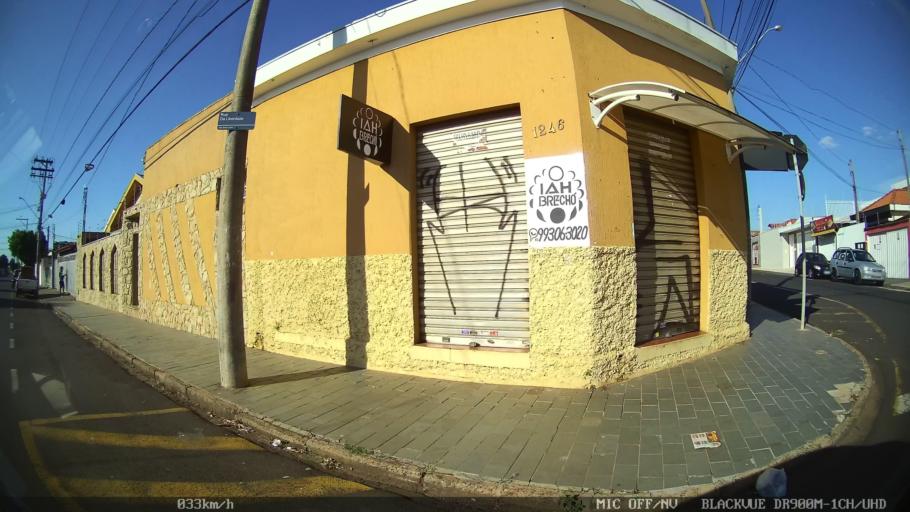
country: BR
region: Sao Paulo
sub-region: Franca
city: Franca
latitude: -20.5306
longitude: -47.4181
